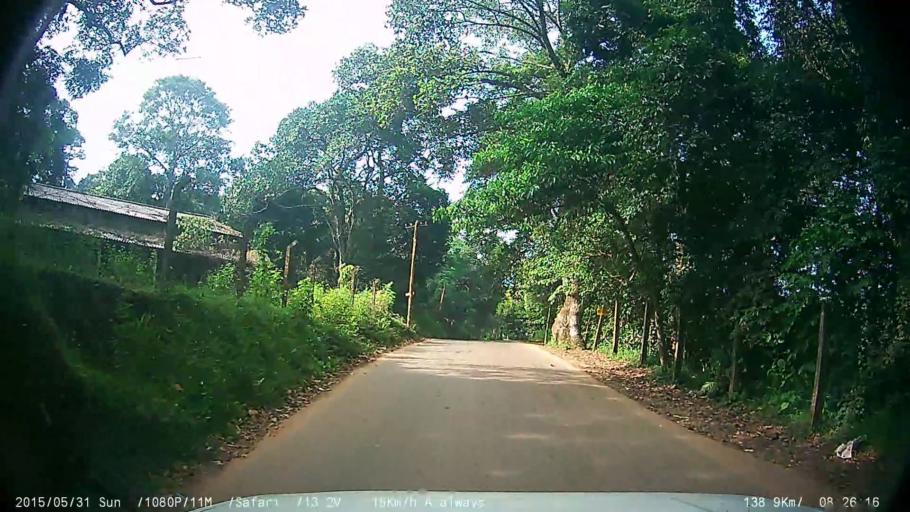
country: IN
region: Kerala
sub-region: Wayanad
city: Kalpetta
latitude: 11.6739
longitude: 75.9576
